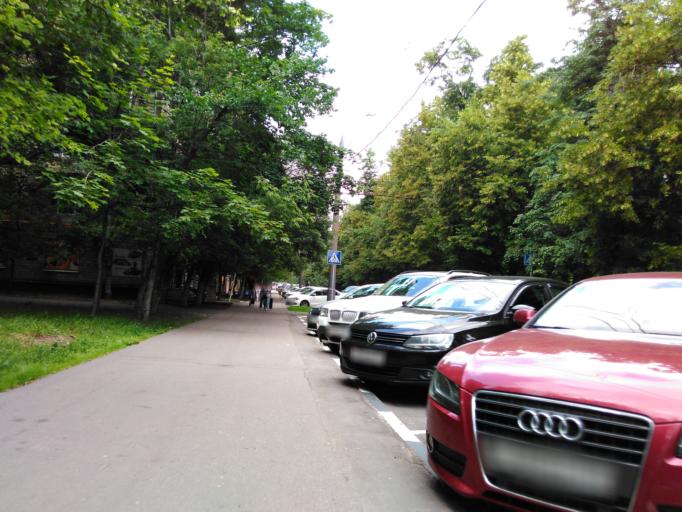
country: RU
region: Moskovskaya
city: Semenovskoye
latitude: 55.6783
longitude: 37.5281
